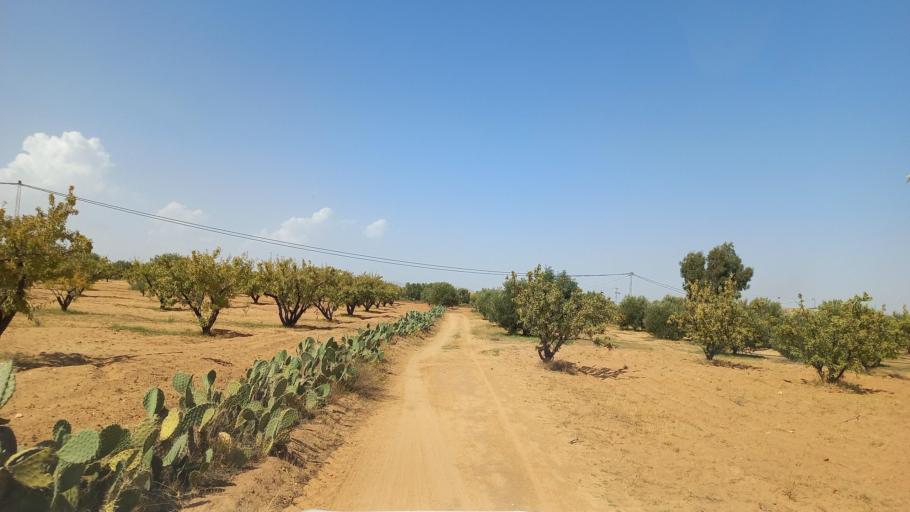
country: TN
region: Al Qasrayn
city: Kasserine
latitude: 35.2234
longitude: 9.0428
